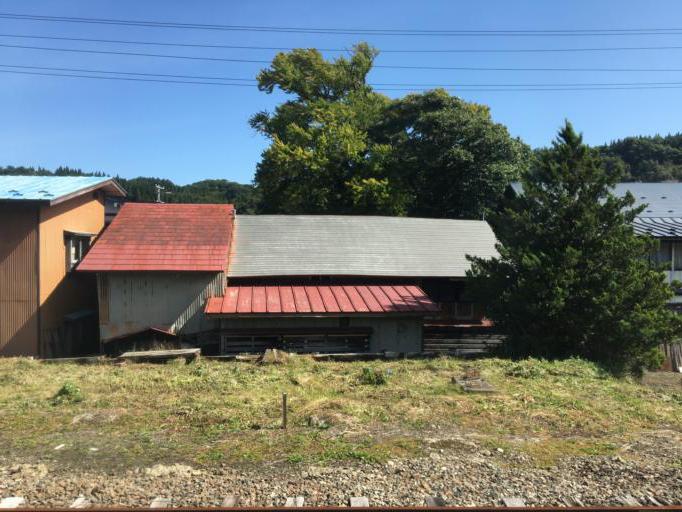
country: JP
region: Iwate
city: Ichinohe
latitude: 40.0979
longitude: 141.0496
